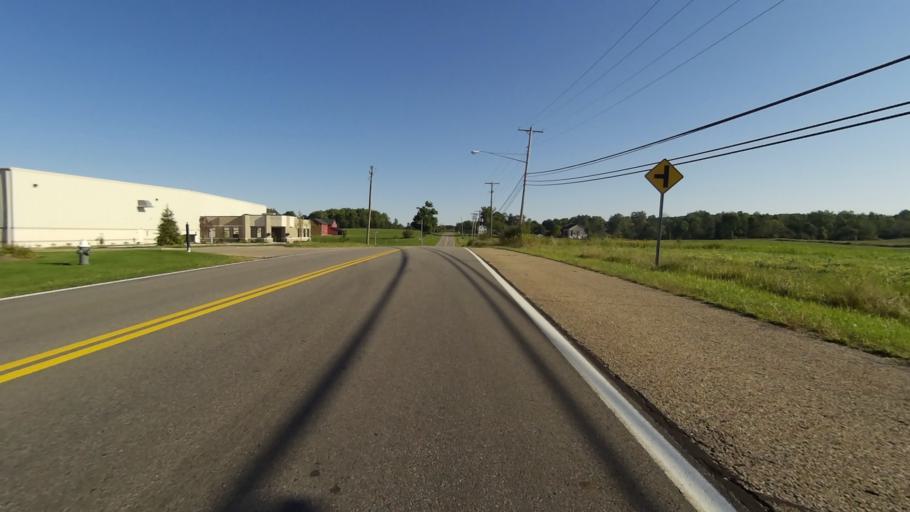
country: US
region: Ohio
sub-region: Portage County
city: Aurora
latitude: 41.2826
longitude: -81.3257
